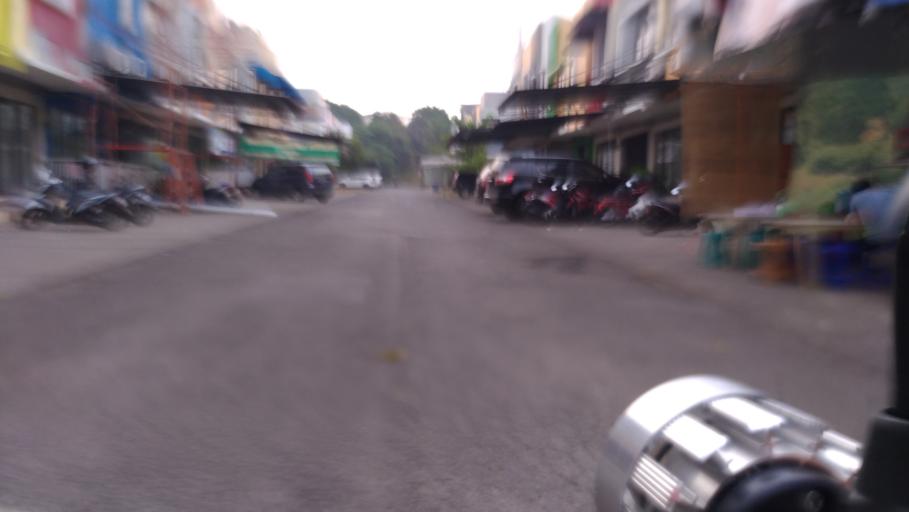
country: ID
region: West Java
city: Cileungsir
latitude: -6.3915
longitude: 106.9471
